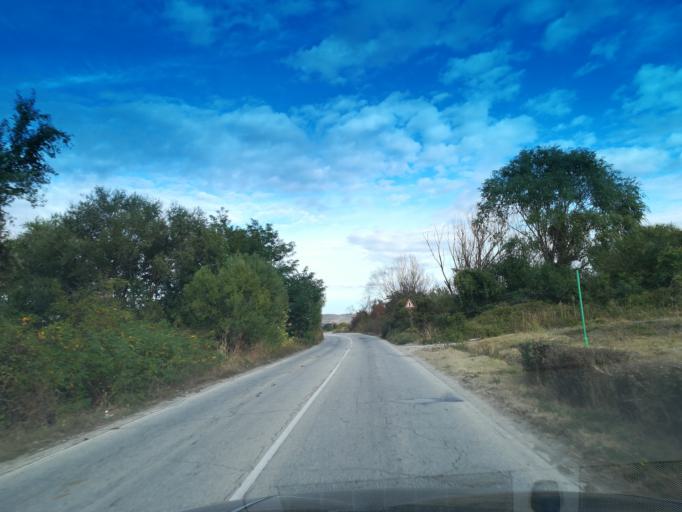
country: BG
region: Pazardzhik
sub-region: Obshtina Bratsigovo
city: Bratsigovo
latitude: 42.0696
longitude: 24.4000
